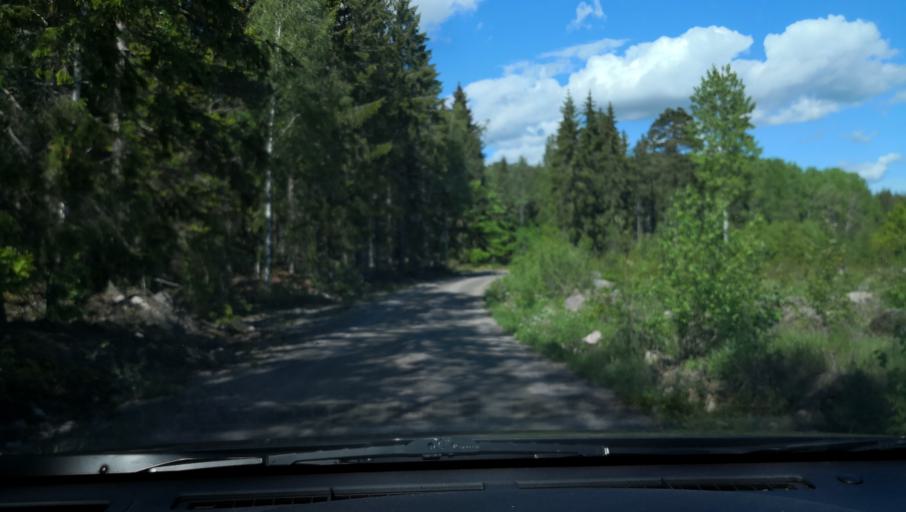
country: SE
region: Vaestmanland
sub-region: Arboga Kommun
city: Tyringe
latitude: 59.3160
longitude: 15.9953
